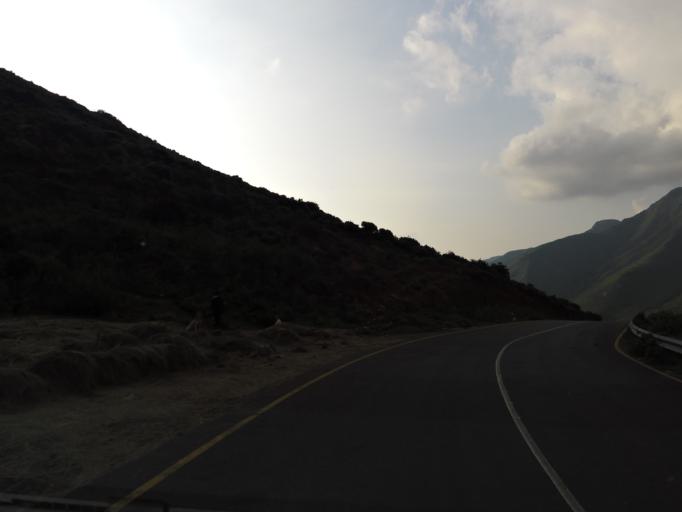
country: LS
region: Butha-Buthe
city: Butha-Buthe
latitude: -29.0602
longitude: 28.3562
